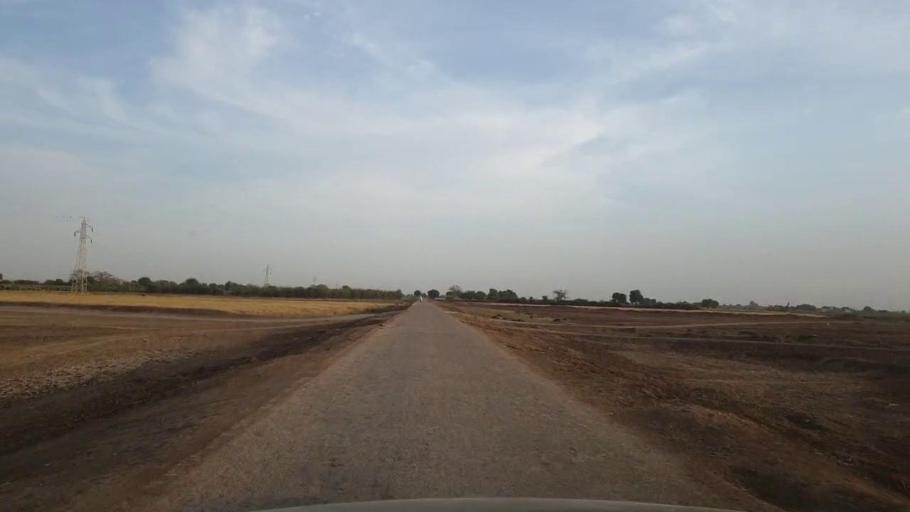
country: PK
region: Sindh
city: Kunri
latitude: 25.1694
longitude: 69.5448
